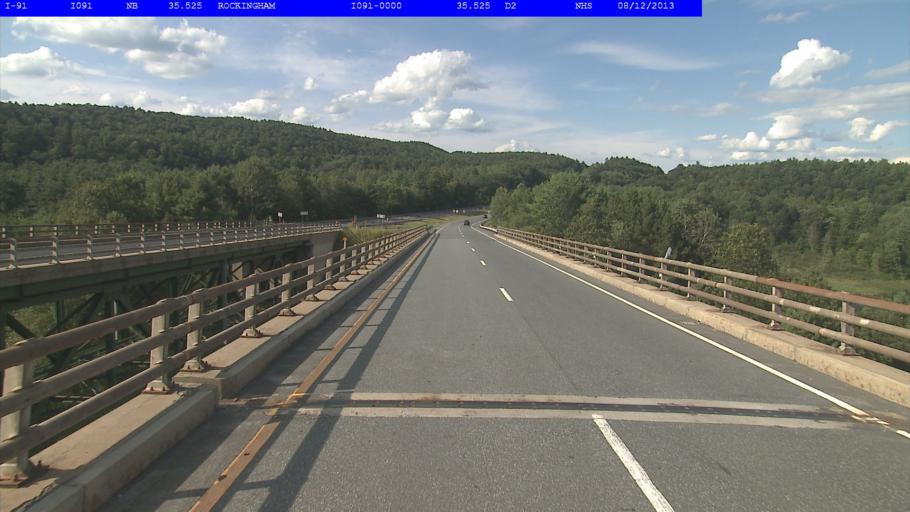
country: US
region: Vermont
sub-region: Windham County
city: Rockingham
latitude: 43.1834
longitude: -72.4629
